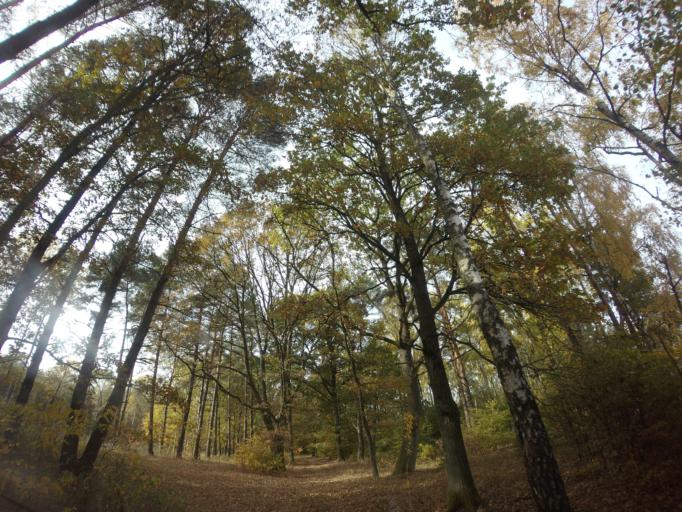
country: PL
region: West Pomeranian Voivodeship
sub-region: Powiat choszczenski
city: Drawno
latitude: 53.2563
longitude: 15.6718
